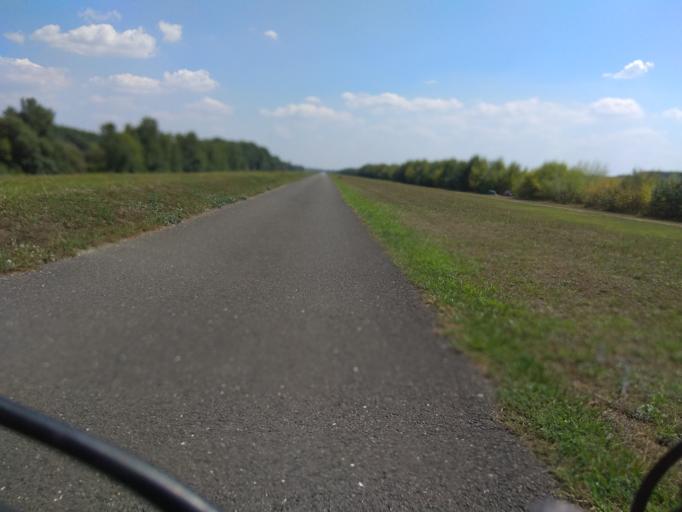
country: SK
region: Trnavsky
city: Gabcikovo
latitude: 47.8537
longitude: 17.5732
